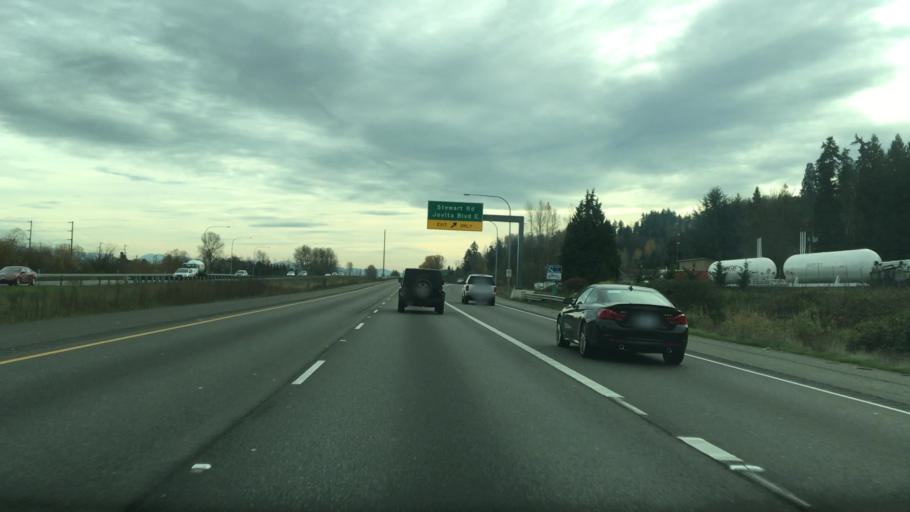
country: US
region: Washington
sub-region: King County
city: Pacific
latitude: 47.2554
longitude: -122.2592
